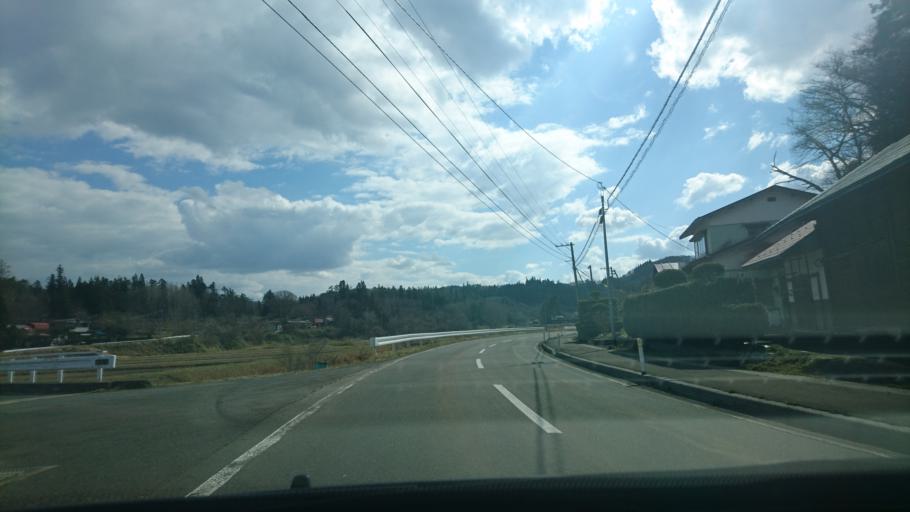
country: JP
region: Iwate
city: Hanamaki
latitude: 39.3450
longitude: 141.2391
